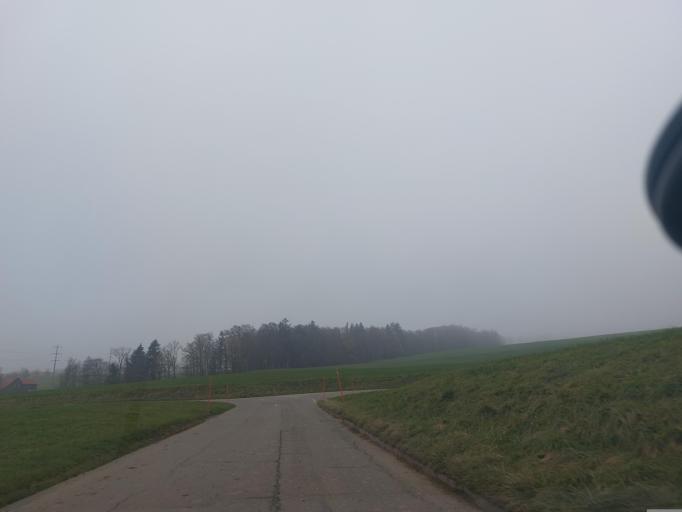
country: CH
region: Fribourg
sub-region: Veveyse District
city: Chatel-Saint-Denis
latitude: 46.5764
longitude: 6.8816
